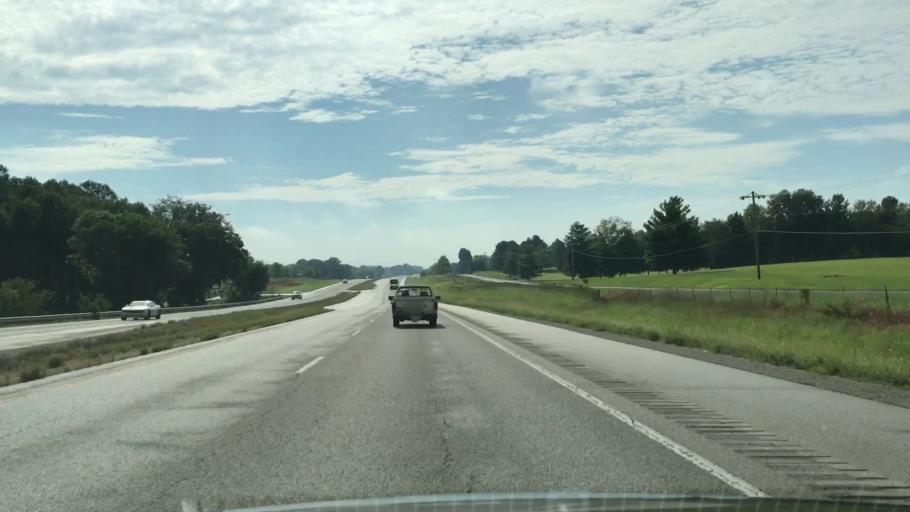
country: US
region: Kentucky
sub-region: Warren County
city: Plano
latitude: 36.8892
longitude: -86.3716
